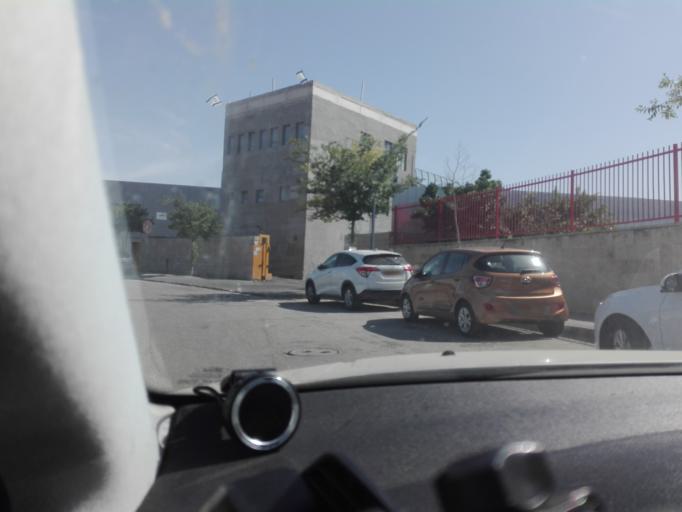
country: IL
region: Central District
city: Bene 'Ayish
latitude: 31.7216
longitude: 34.7590
